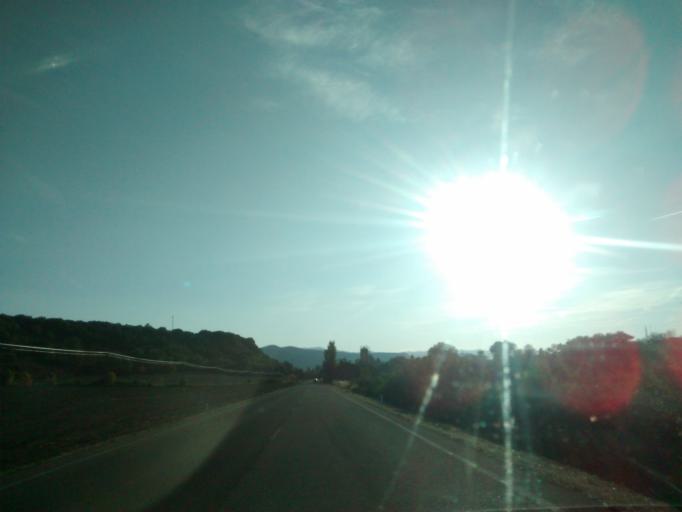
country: ES
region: Aragon
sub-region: Provincia de Huesca
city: Santa Cruz de la Seros
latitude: 42.5788
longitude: -0.7478
